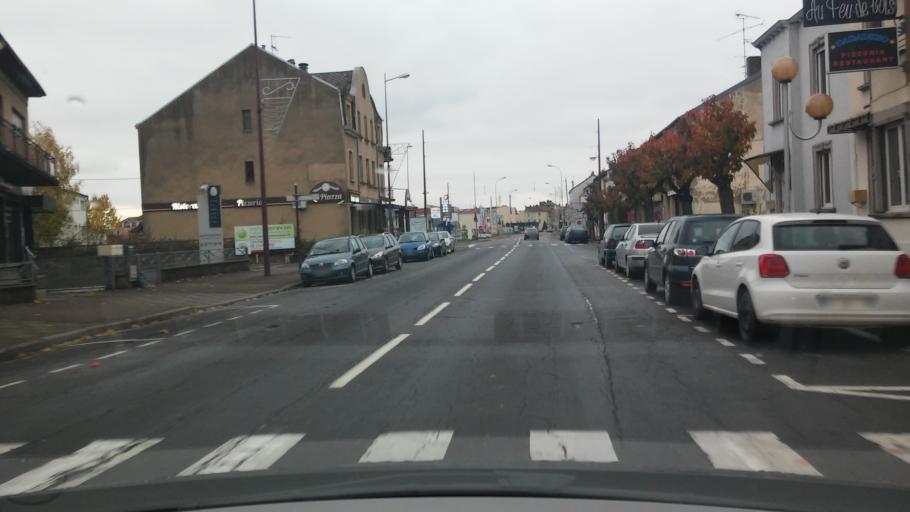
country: FR
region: Lorraine
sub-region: Departement de la Moselle
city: Talange
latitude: 49.2416
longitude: 6.1692
